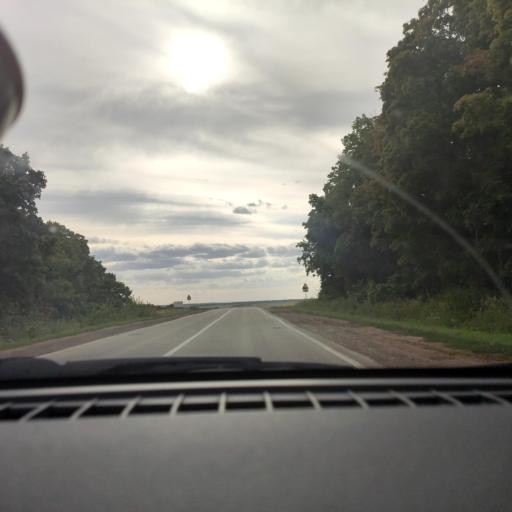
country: RU
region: Samara
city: Kinel'
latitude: 53.4415
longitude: 50.6325
